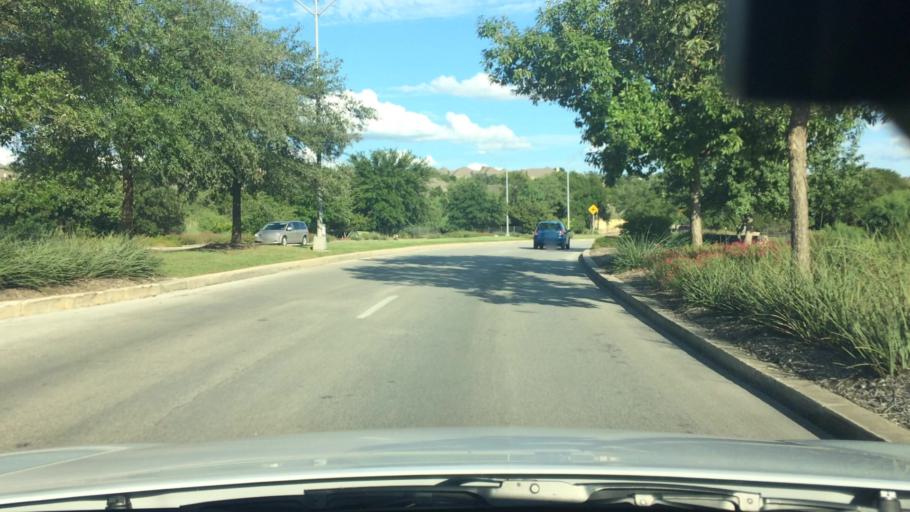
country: US
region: Texas
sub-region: Bexar County
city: Timberwood Park
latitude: 29.6616
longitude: -98.4325
